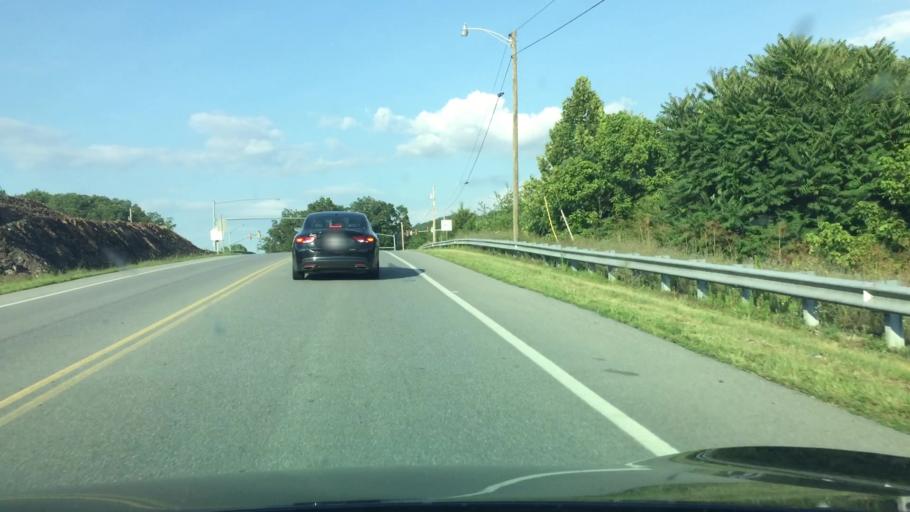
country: US
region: Virginia
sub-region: City of Radford
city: Radford
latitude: 37.1212
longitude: -80.5349
